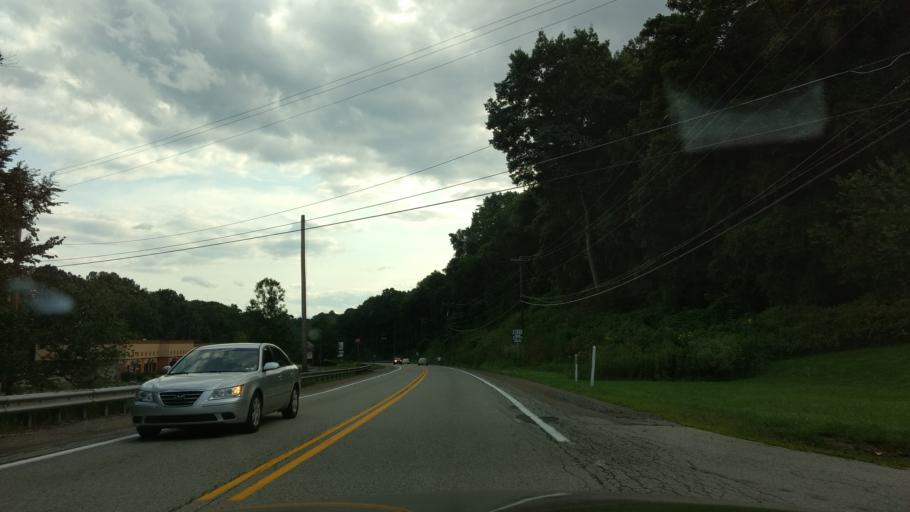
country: US
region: Pennsylvania
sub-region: Allegheny County
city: Plum
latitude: 40.4807
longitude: -79.7050
